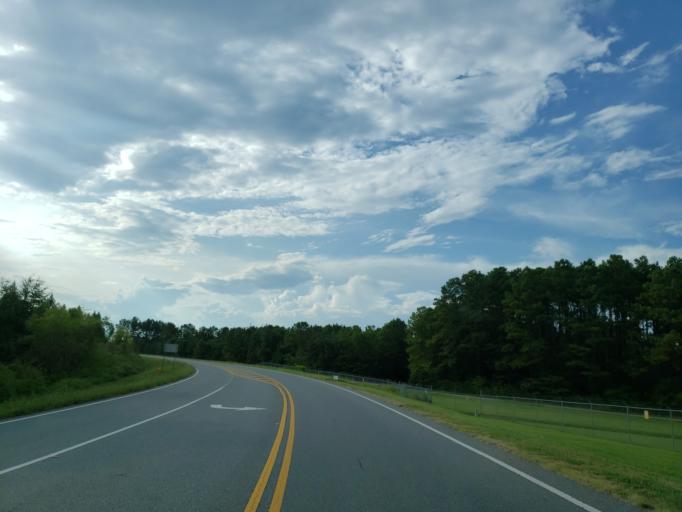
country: US
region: Georgia
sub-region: Bartow County
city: Euharlee
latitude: 34.1173
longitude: -84.9270
